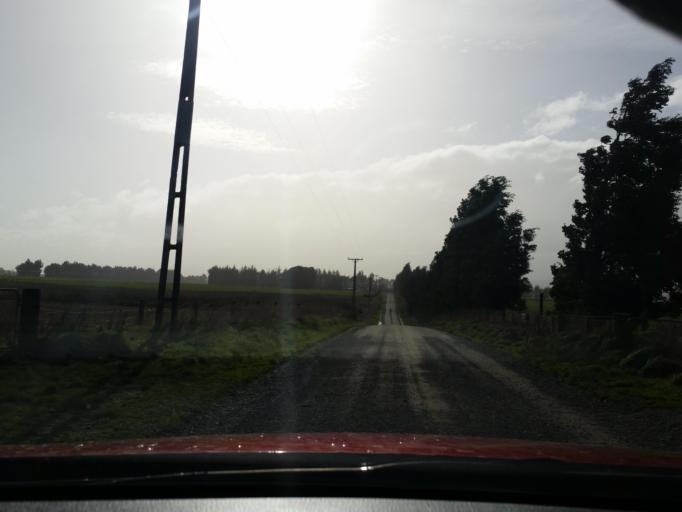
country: NZ
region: Southland
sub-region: Invercargill City
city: Invercargill
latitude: -46.2873
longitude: 168.4098
